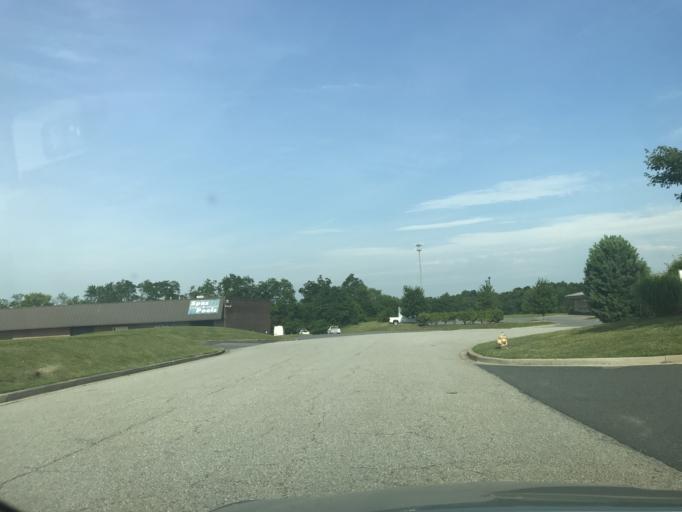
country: US
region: Maryland
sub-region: Harford County
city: Bel Air North
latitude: 39.5680
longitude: -76.3607
